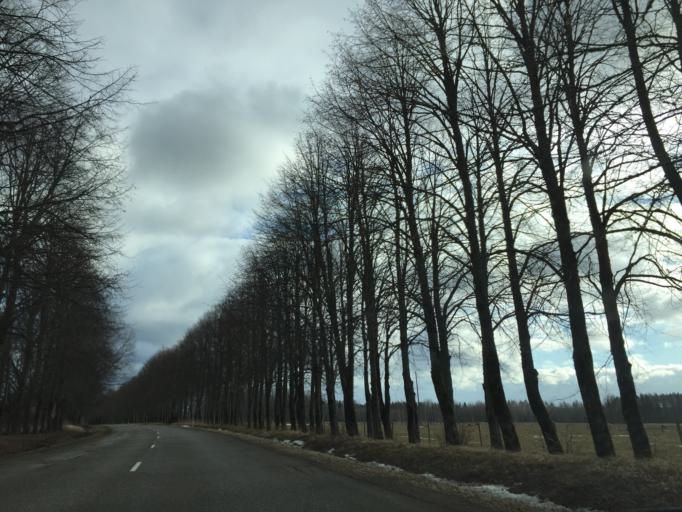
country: LV
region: Aloja
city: Staicele
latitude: 57.8812
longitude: 24.6610
